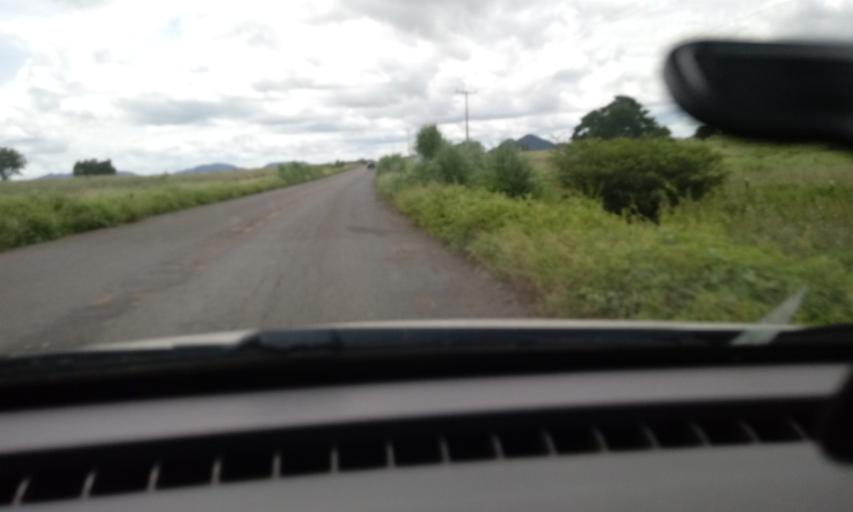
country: BR
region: Bahia
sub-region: Guanambi
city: Guanambi
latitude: -14.1035
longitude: -42.8695
